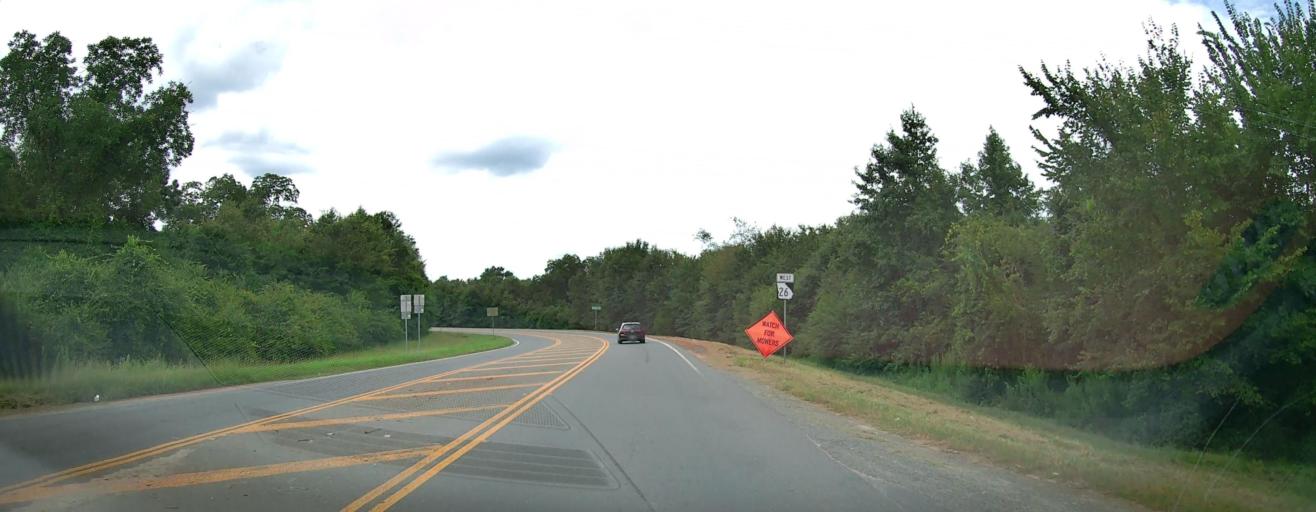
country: US
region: Georgia
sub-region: Macon County
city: Oglethorpe
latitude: 32.2696
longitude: -84.0819
